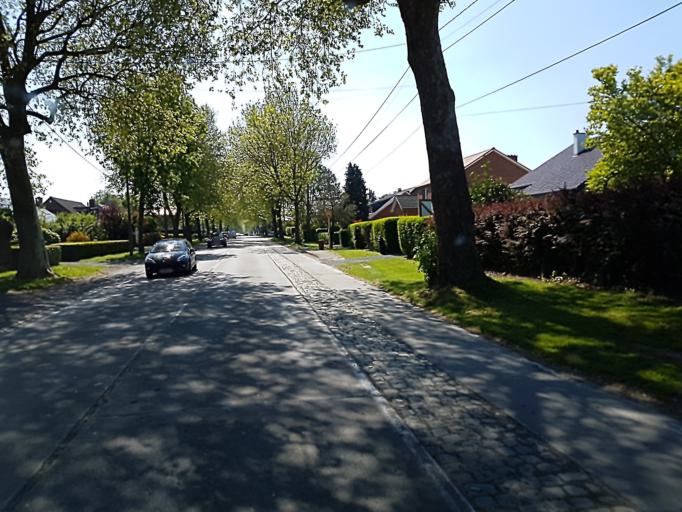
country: BE
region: Wallonia
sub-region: Province du Hainaut
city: Jurbise
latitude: 50.5224
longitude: 3.9167
